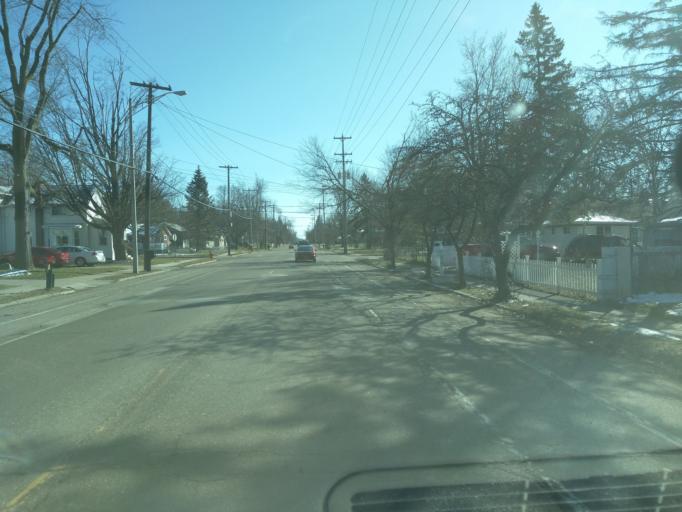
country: US
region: Michigan
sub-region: Ingham County
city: Lansing
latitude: 42.6954
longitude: -84.5823
